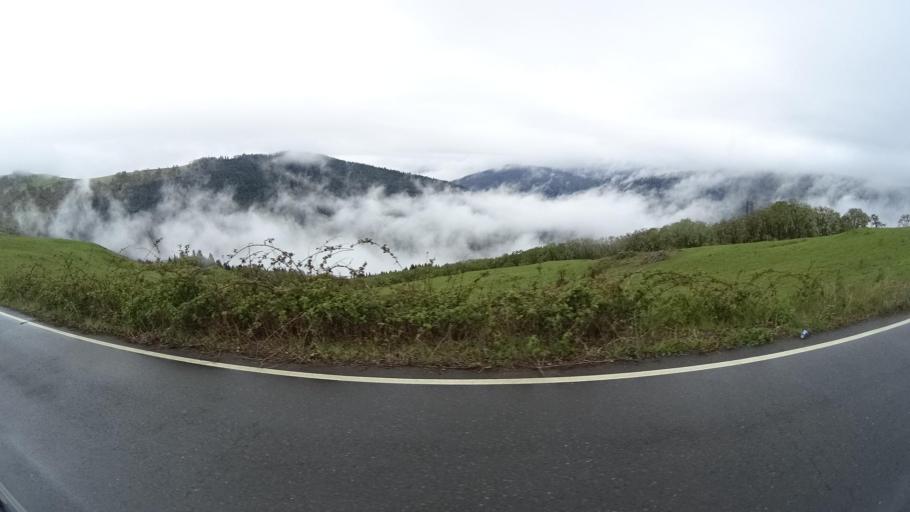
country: US
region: California
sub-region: Humboldt County
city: Westhaven-Moonstone
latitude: 41.1653
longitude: -123.9106
